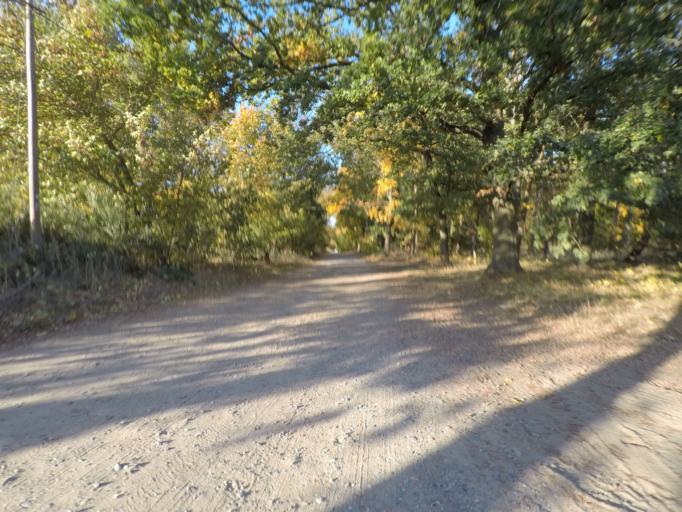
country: DE
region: Brandenburg
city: Biesenthal
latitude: 52.7750
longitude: 13.6416
